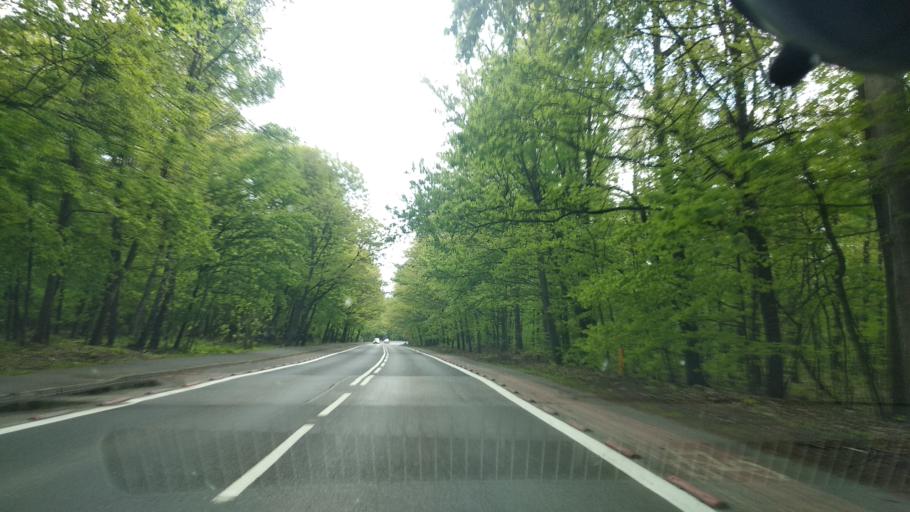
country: PL
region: Silesian Voivodeship
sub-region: Ruda Slaska
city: Ruda Slaska
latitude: 50.2361
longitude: 18.9109
